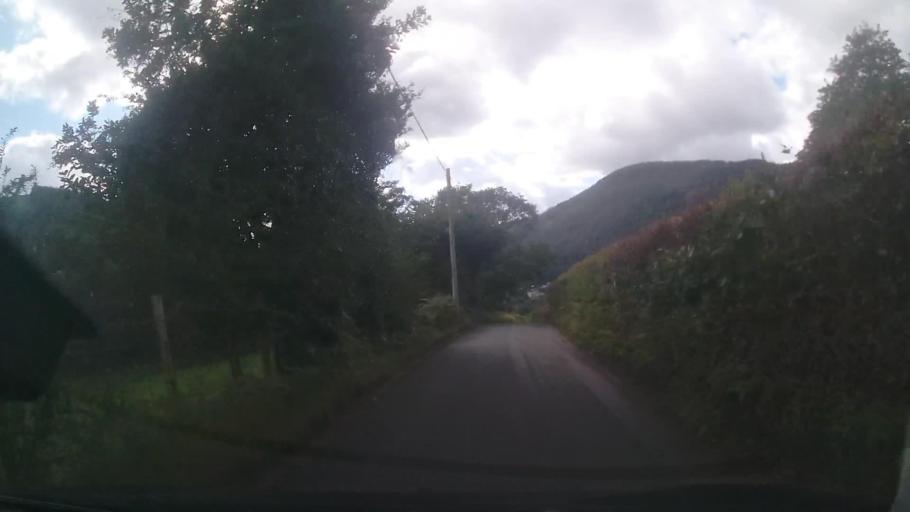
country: GB
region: Wales
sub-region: Gwynedd
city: Corris
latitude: 52.7247
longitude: -3.6841
